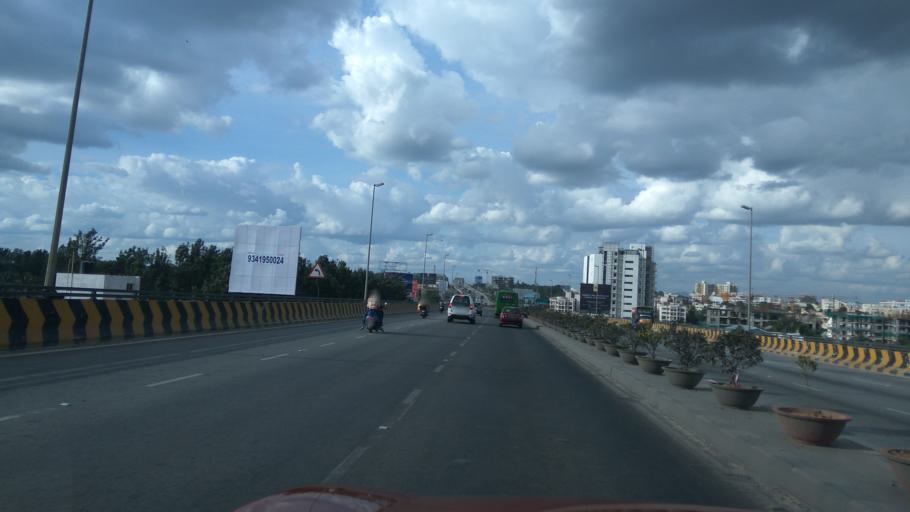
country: IN
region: Karnataka
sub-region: Bangalore Urban
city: Yelahanka
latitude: 13.0589
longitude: 77.5934
